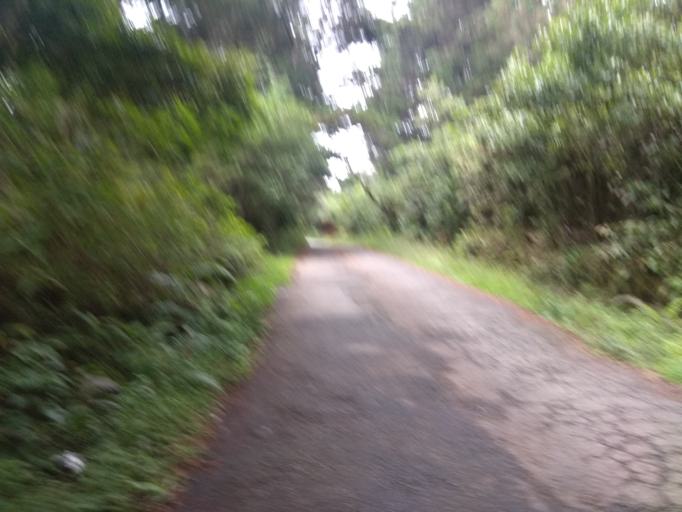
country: CR
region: Heredia
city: San Josecito
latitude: 10.0698
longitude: -84.0834
